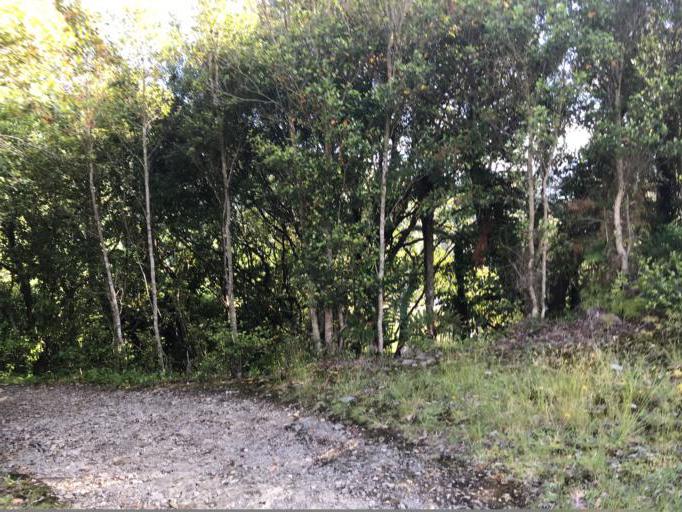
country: NZ
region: Wellington
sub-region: Kapiti Coast District
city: Otaki
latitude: -40.8712
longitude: 175.2318
